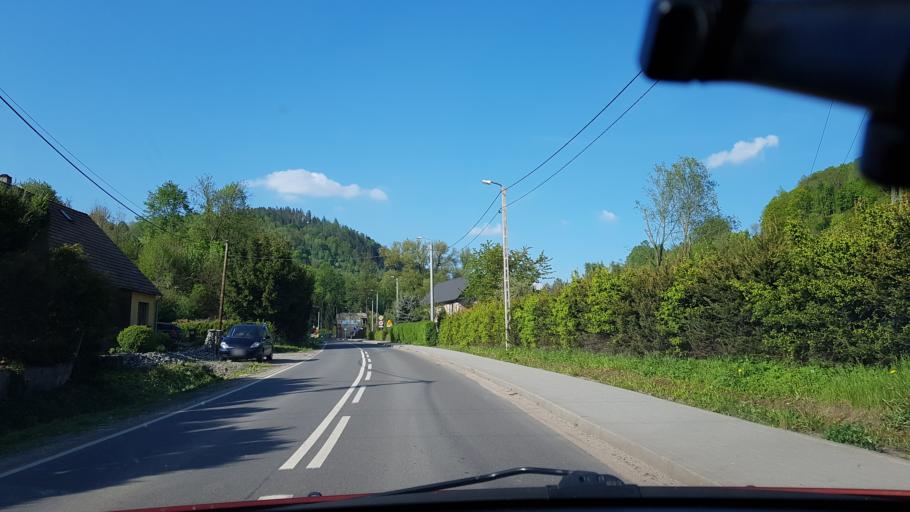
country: PL
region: Lower Silesian Voivodeship
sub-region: Powiat klodzki
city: Nowa Ruda
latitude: 50.5723
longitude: 16.4746
